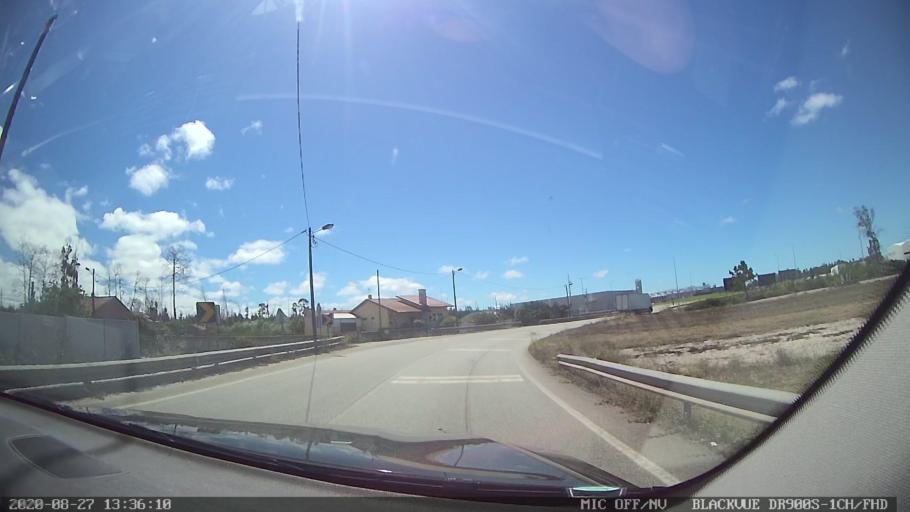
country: PT
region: Coimbra
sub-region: Mira
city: Mira
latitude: 40.4579
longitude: -8.7025
